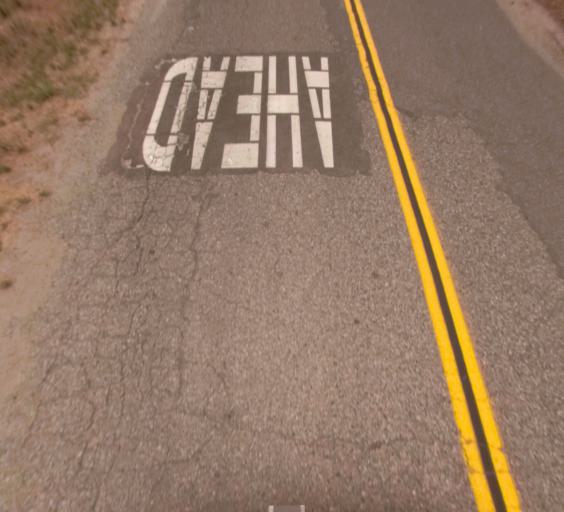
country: US
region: California
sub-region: Madera County
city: Oakhurst
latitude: 37.3638
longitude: -119.6156
